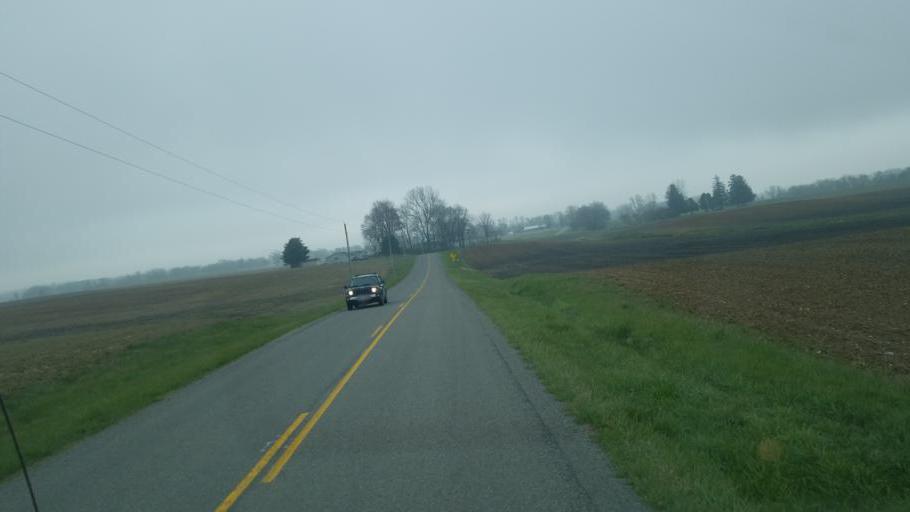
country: US
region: Ohio
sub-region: Logan County
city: Bellefontaine
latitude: 40.4031
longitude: -83.8136
